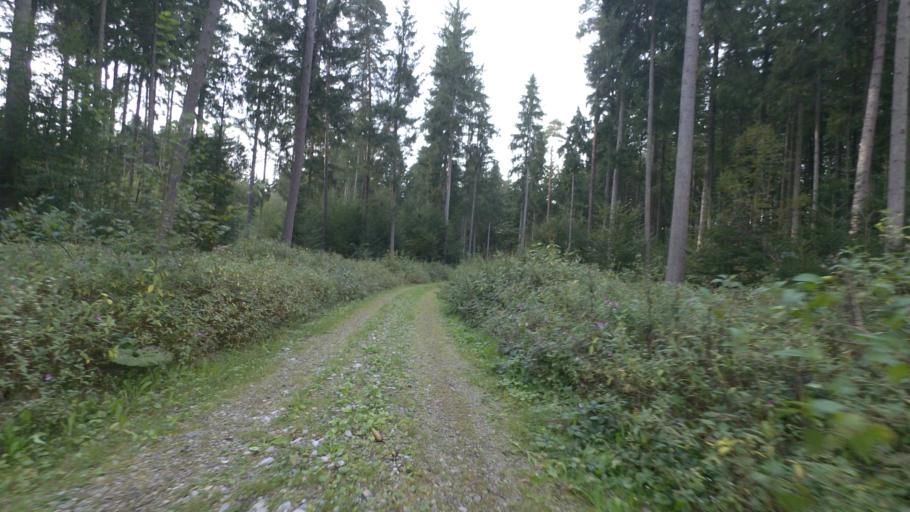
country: DE
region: Bavaria
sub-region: Upper Bavaria
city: Chieming
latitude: 47.9175
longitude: 12.5504
